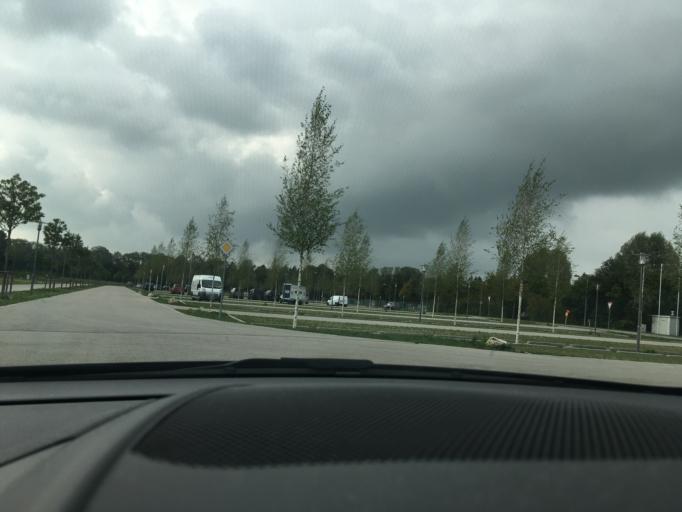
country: DE
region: Bavaria
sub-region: Upper Bavaria
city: Ismaning
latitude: 48.2405
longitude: 11.6867
